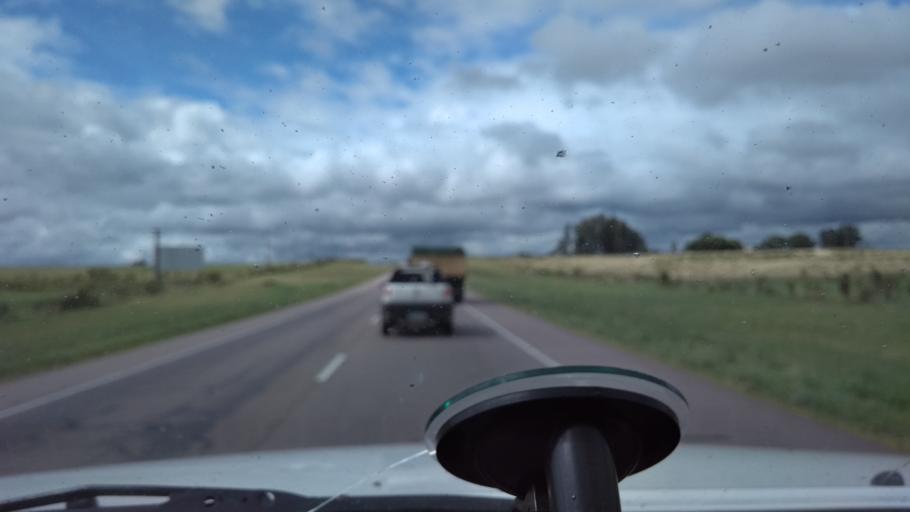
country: UY
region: Florida
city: Florida
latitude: -34.1829
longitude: -56.1932
